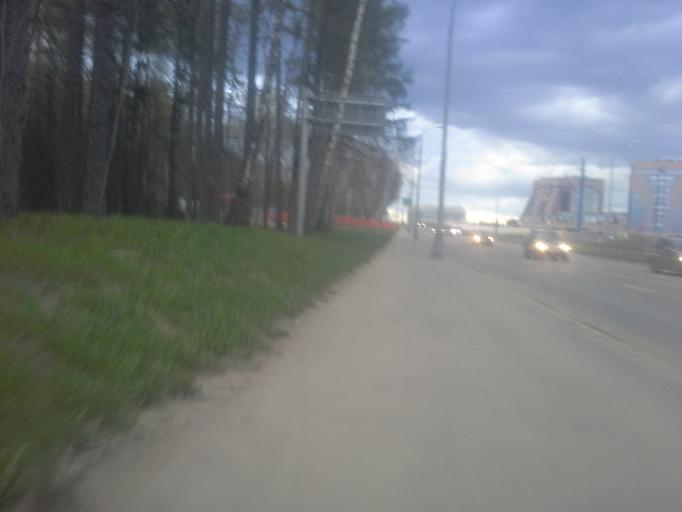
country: RU
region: Moskovskaya
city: Kommunarka
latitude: 55.5785
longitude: 37.4626
